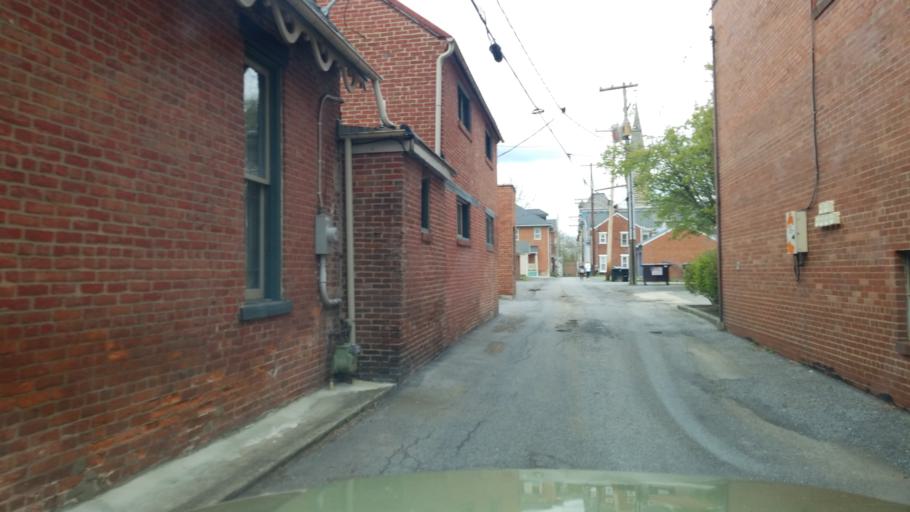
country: US
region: Pennsylvania
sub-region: Blair County
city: Hollidaysburg
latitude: 40.4296
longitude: -78.3949
